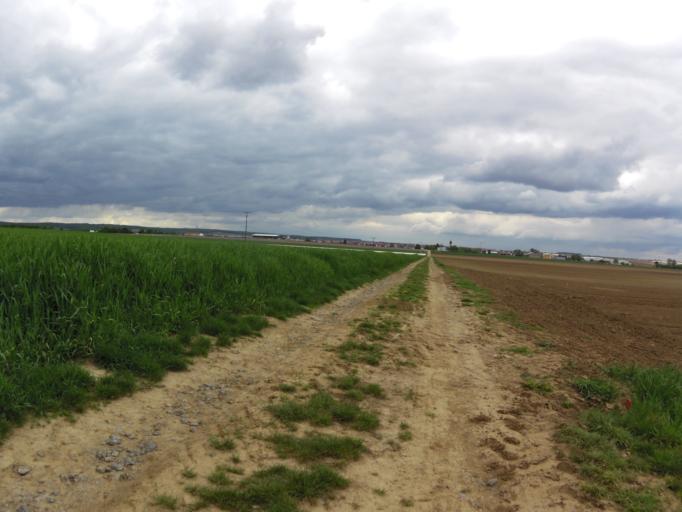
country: DE
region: Bavaria
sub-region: Regierungsbezirk Unterfranken
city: Unterpleichfeld
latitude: 49.8563
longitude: 10.0495
